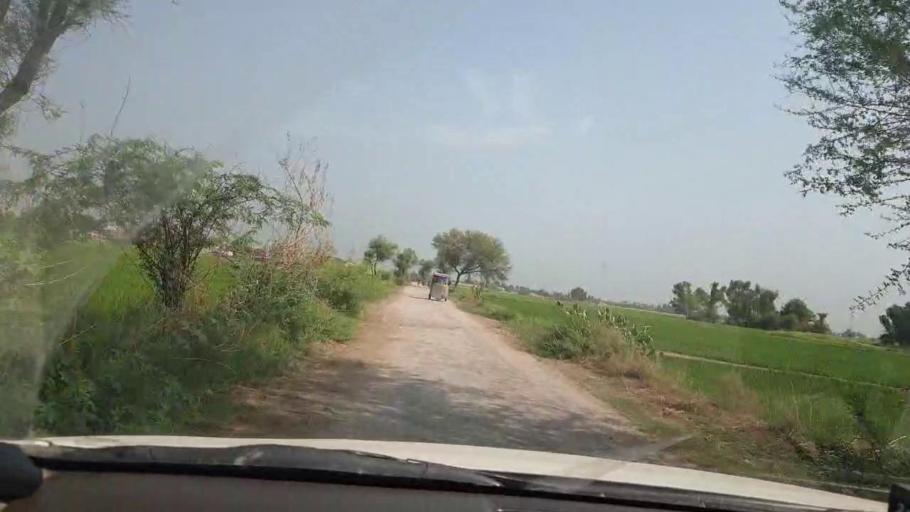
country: PK
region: Sindh
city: Chak
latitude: 27.8344
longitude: 68.7990
